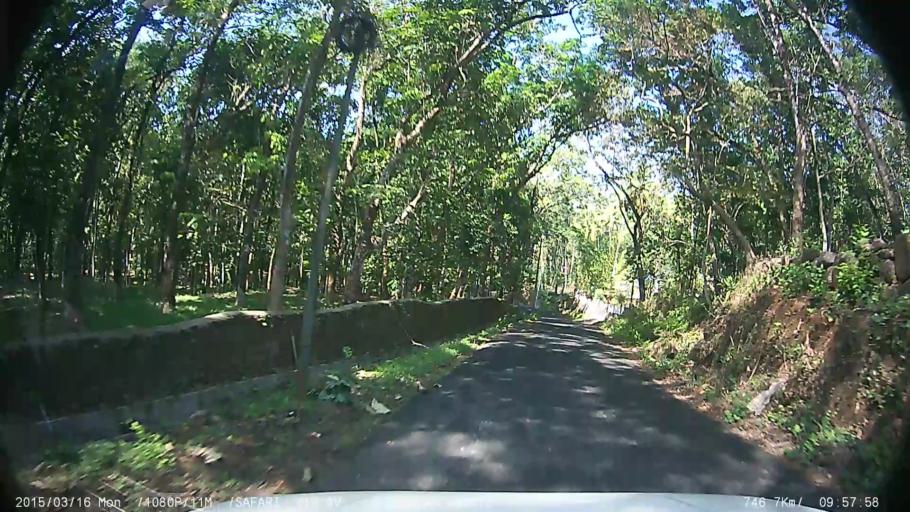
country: IN
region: Kerala
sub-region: Kottayam
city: Palackattumala
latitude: 9.7868
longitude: 76.6035
